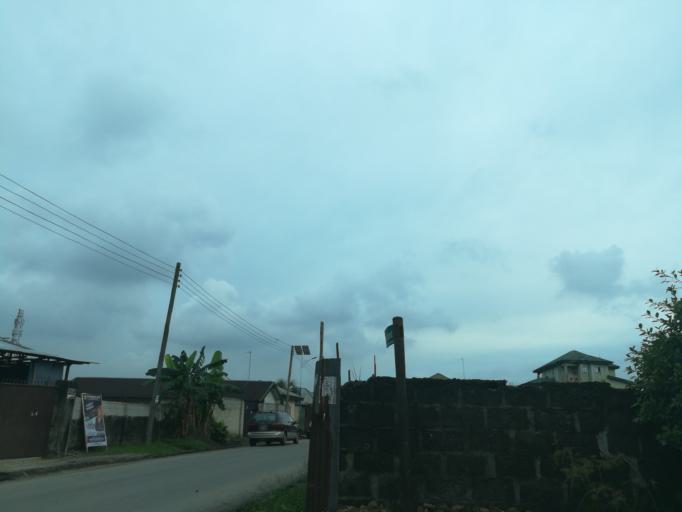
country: NG
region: Rivers
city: Port Harcourt
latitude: 4.8085
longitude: 6.9910
